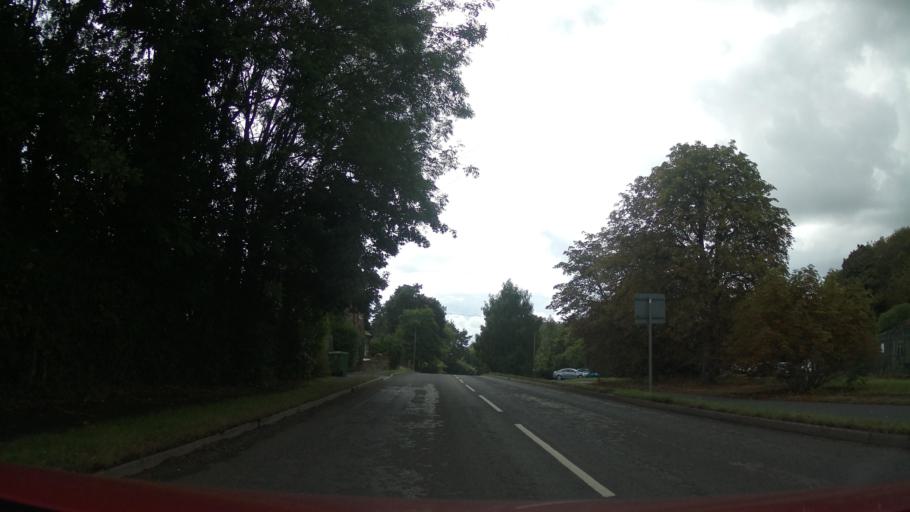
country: GB
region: England
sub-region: Staffordshire
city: Eccleshall
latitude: 52.8921
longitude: -2.2168
